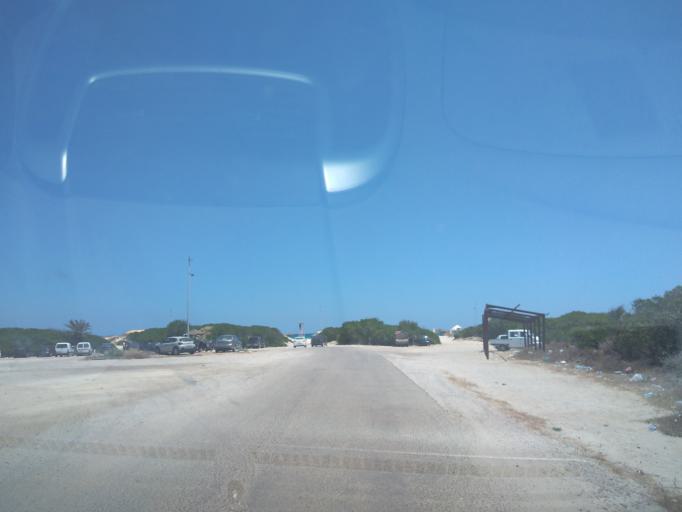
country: TN
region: Susah
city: Harqalah
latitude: 36.1330
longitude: 10.4654
